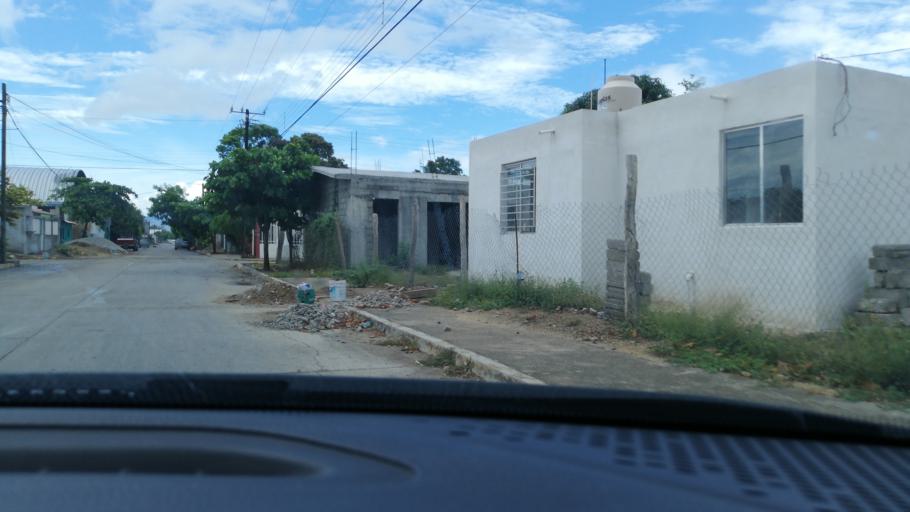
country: MX
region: Oaxaca
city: Asuncion Ixtaltepec
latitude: 16.5084
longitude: -95.0500
